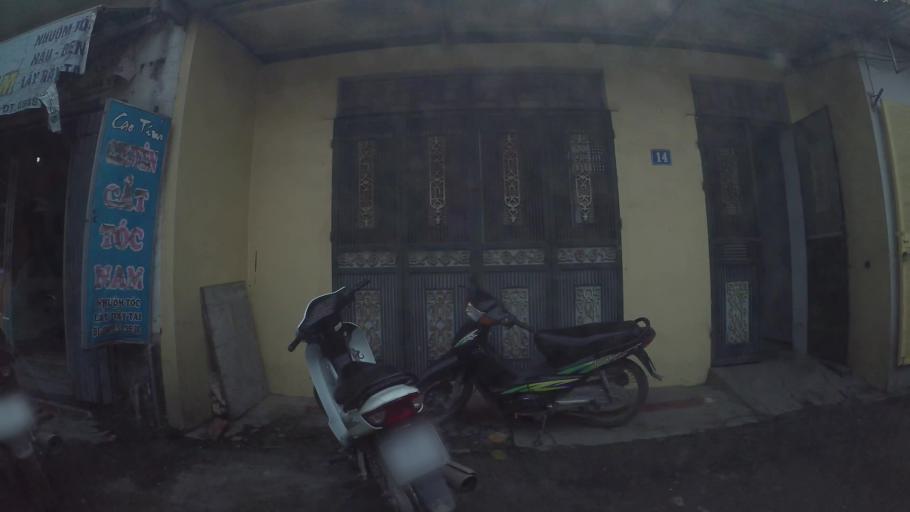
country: VN
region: Ha Noi
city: Van Dien
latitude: 20.9649
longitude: 105.8664
